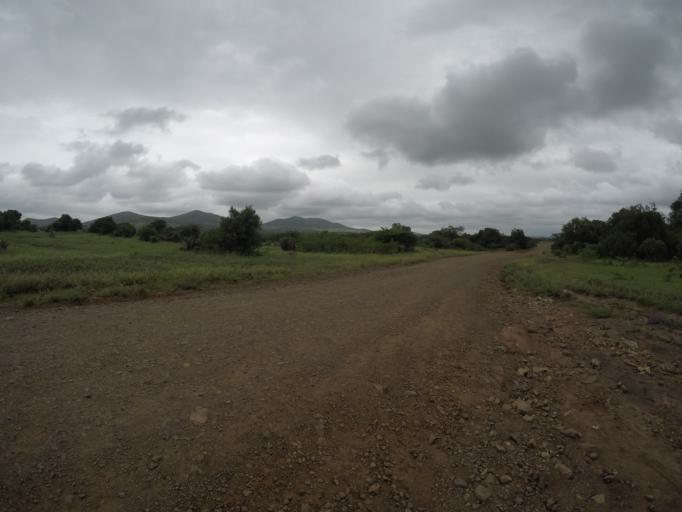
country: ZA
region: KwaZulu-Natal
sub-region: uThungulu District Municipality
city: Empangeni
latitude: -28.6101
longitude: 31.8641
